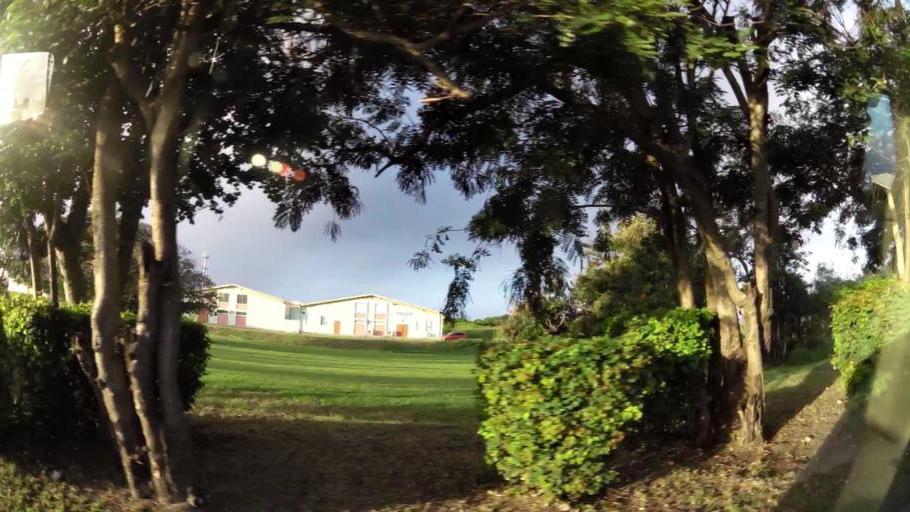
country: BB
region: Saint Philip
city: Crane
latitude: 13.1175
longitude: -59.4721
